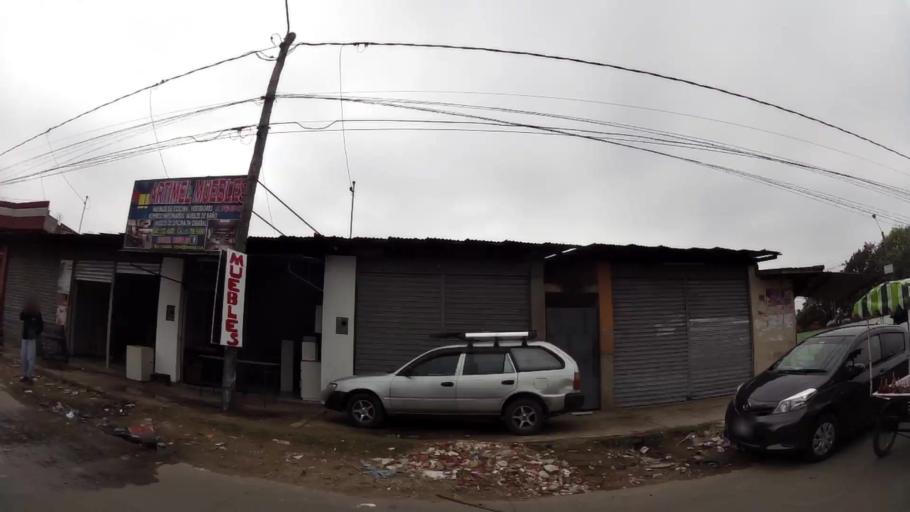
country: BO
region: Santa Cruz
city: Santa Cruz de la Sierra
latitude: -17.8294
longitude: -63.1727
